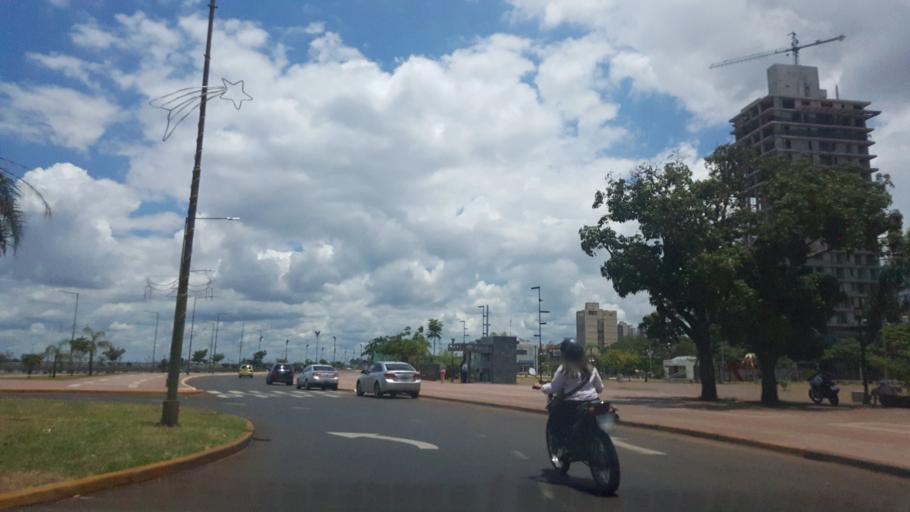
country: AR
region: Misiones
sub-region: Departamento de Capital
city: Posadas
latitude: -27.3680
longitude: -55.8846
